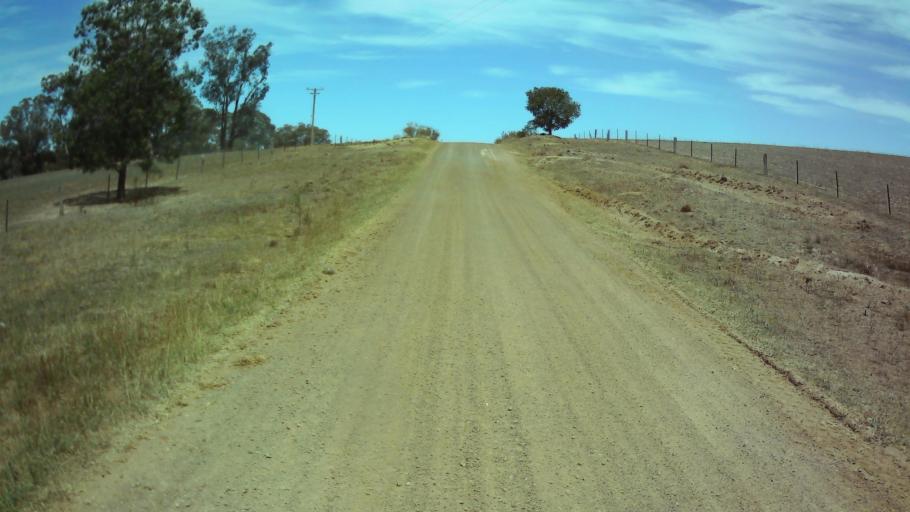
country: AU
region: New South Wales
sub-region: Weddin
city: Grenfell
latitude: -33.8221
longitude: 148.1685
